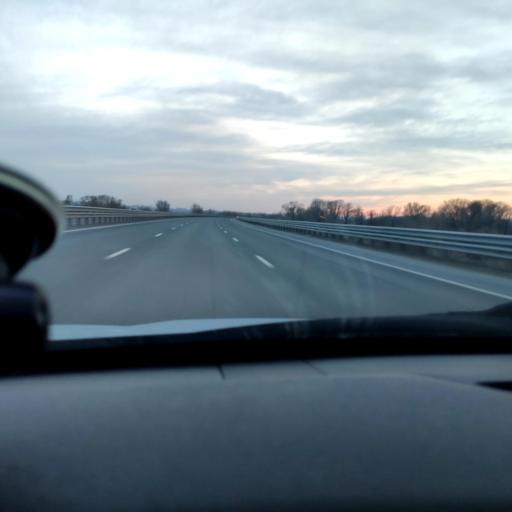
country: RU
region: Samara
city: Smyshlyayevka
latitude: 53.1629
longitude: 50.3237
